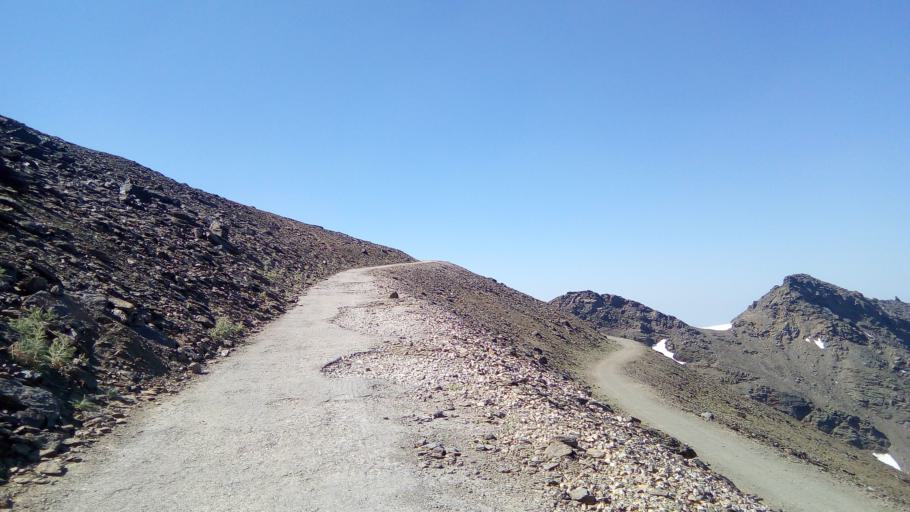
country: ES
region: Andalusia
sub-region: Provincia de Granada
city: Capileira
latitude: 37.0538
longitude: -3.3712
